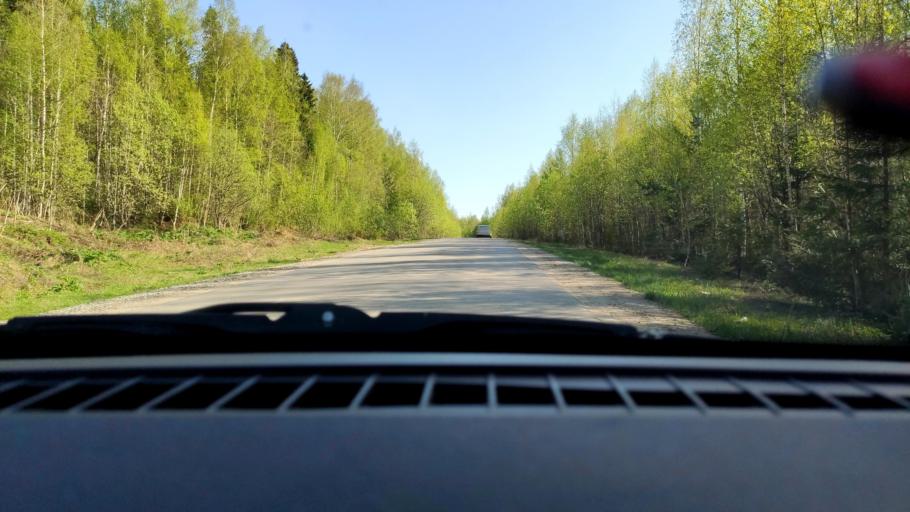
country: RU
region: Perm
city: Kondratovo
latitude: 58.0656
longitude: 56.0021
